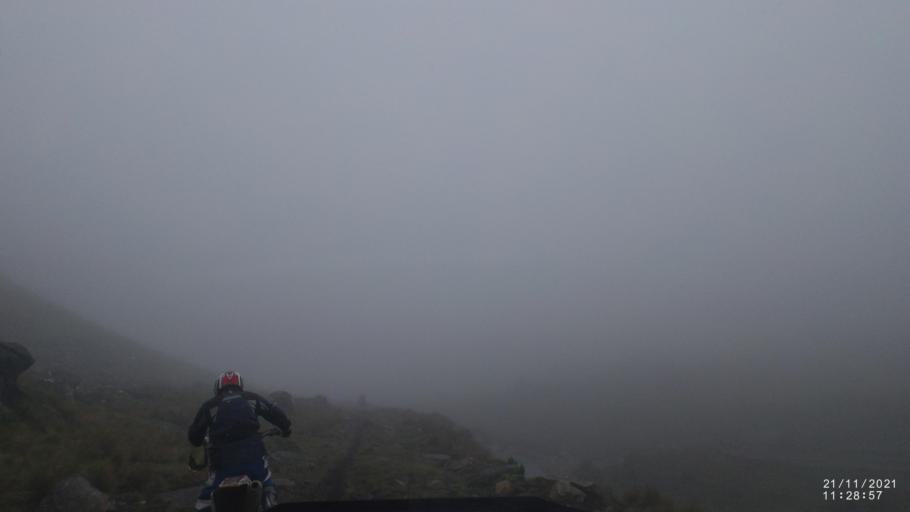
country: BO
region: Cochabamba
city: Cochabamba
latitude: -16.9614
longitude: -66.2681
